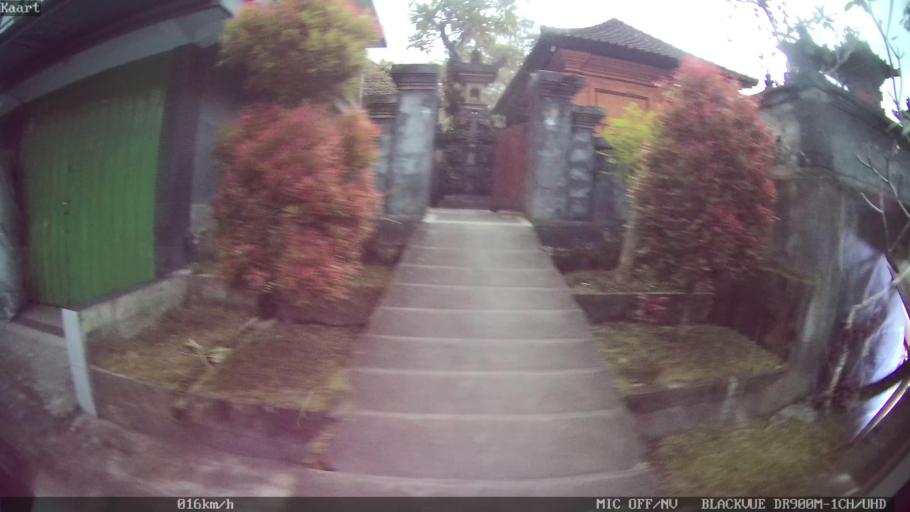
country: ID
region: Bali
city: Banjar Petak
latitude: -8.4478
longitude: 115.3233
